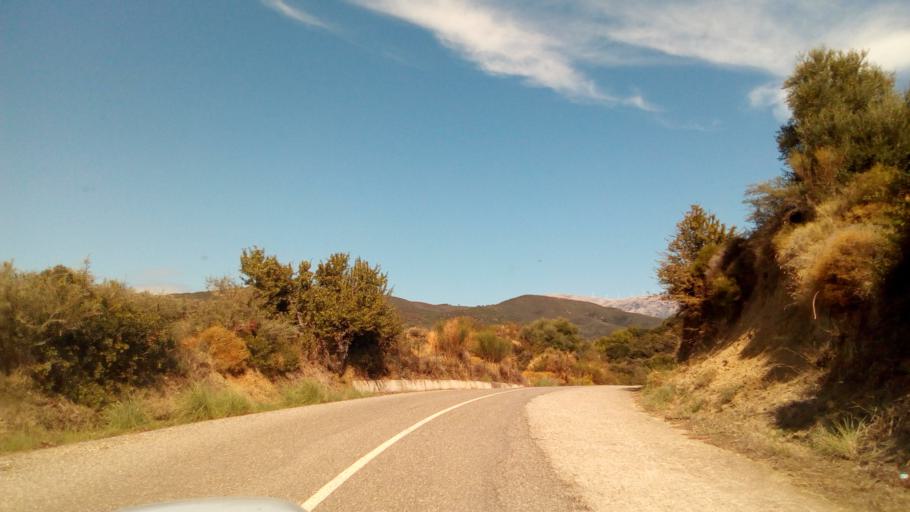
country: GR
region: West Greece
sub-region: Nomos Aitolias kai Akarnanias
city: Antirrio
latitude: 38.3492
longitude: 21.7542
